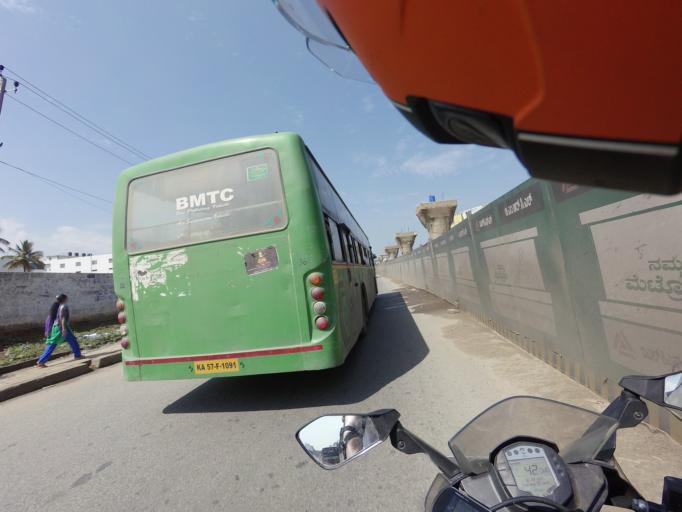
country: IN
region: Karnataka
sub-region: Bangalore Urban
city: Bangalore
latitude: 12.9287
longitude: 77.5034
